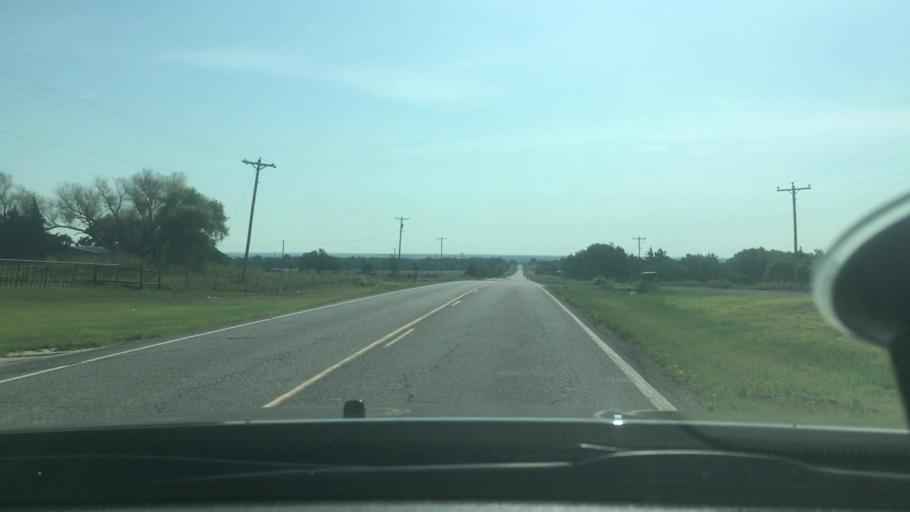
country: US
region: Oklahoma
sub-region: Garvin County
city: Wynnewood
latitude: 34.6518
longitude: -97.2448
